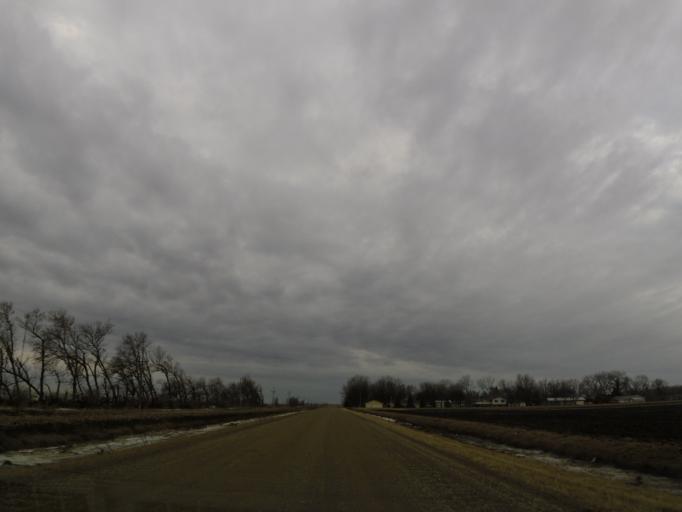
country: US
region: North Dakota
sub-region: Walsh County
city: Grafton
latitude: 48.4197
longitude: -97.4283
